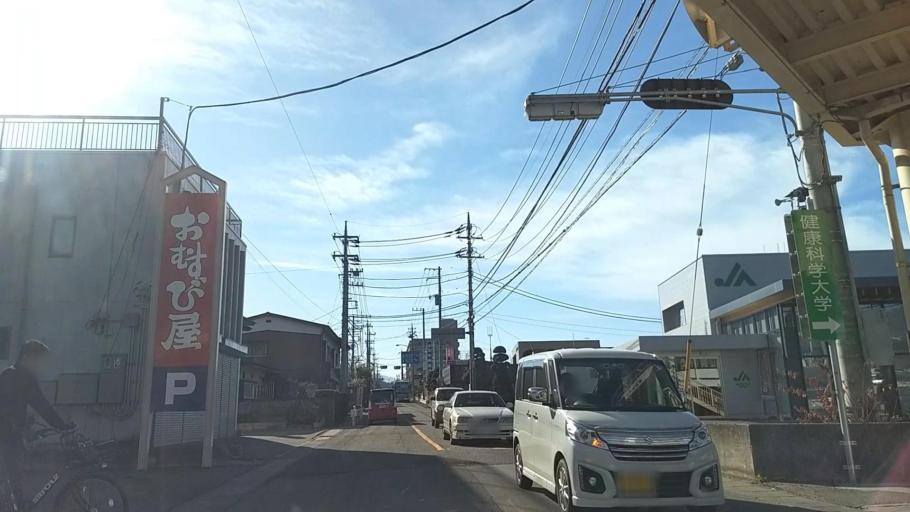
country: JP
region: Yamanashi
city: Otsuki
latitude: 35.5744
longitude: 138.9293
